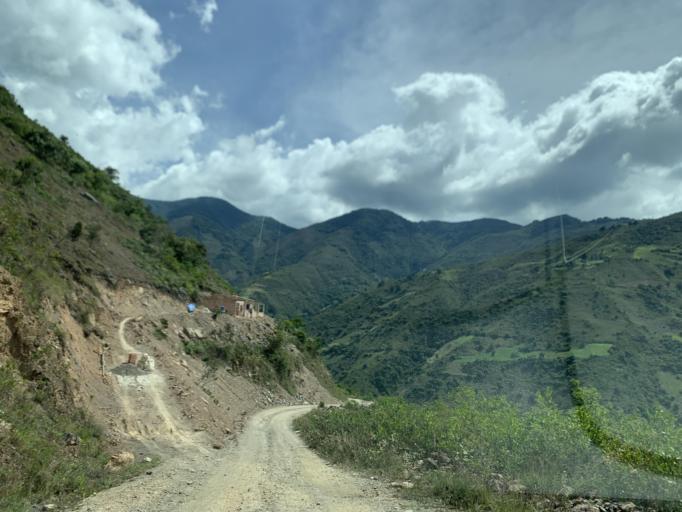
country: CO
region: Boyaca
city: Tipacoque
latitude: 6.4514
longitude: -72.7071
